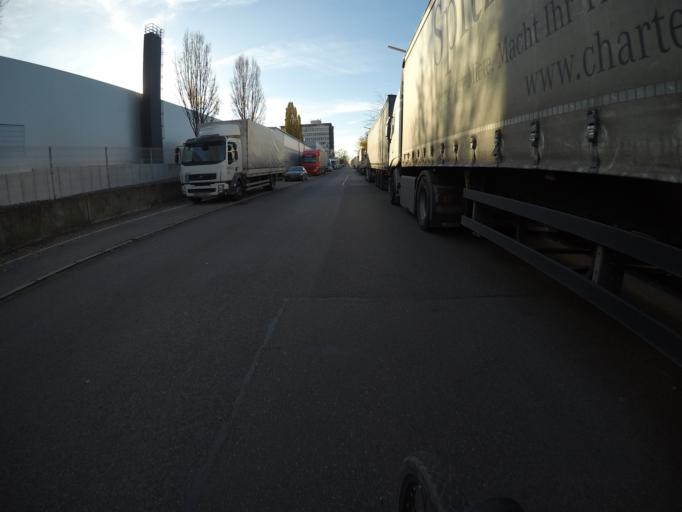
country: DE
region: Baden-Wuerttemberg
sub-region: Regierungsbezirk Stuttgart
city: Fellbach
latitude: 48.8167
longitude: 9.2622
